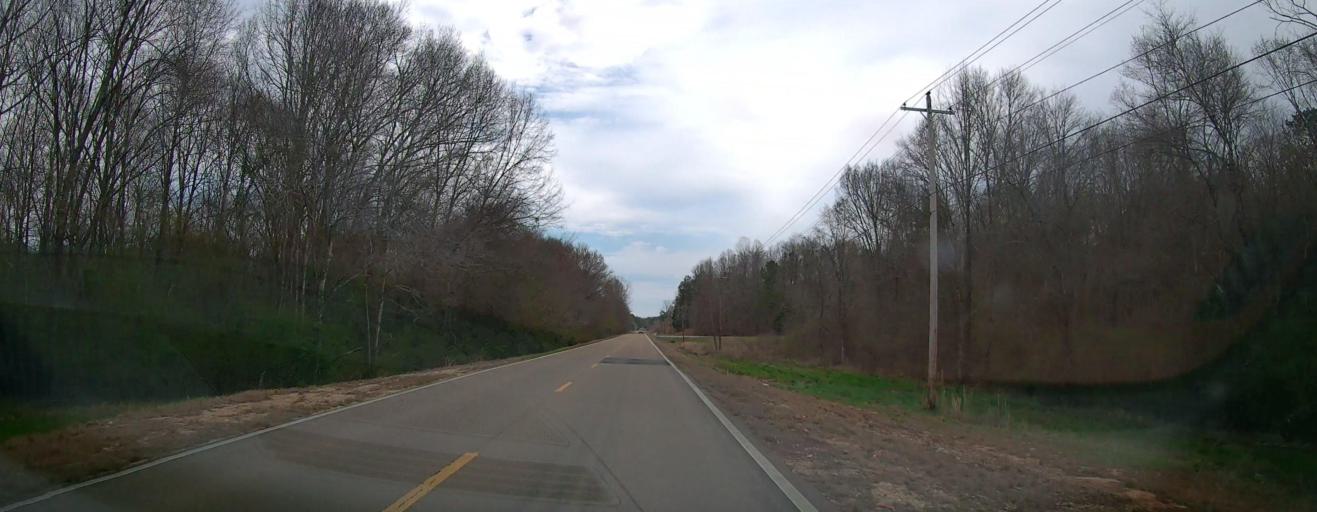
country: US
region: Mississippi
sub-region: Itawamba County
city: Fulton
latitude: 34.2576
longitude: -88.3166
